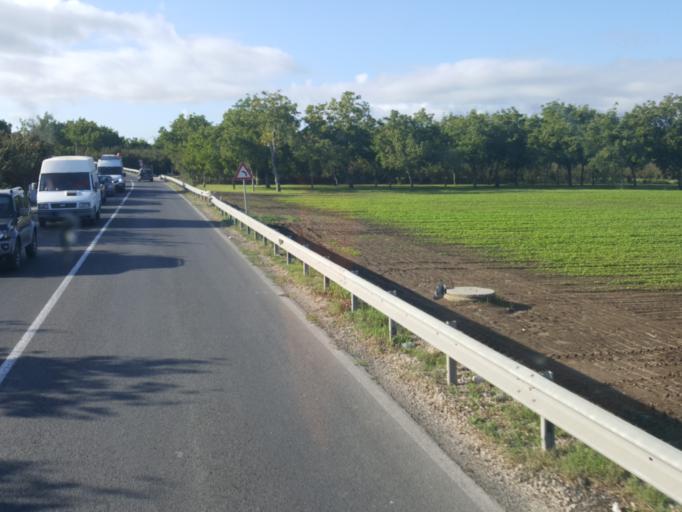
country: IT
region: Campania
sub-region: Provincia di Napoli
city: Nola
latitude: 40.9263
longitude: 14.5105
